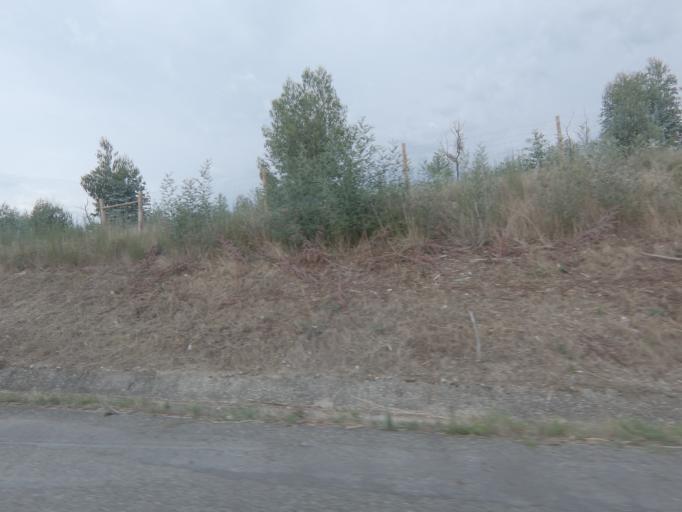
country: PT
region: Viseu
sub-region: Concelho de Tondela
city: Tondela
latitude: 40.5152
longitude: -8.0924
